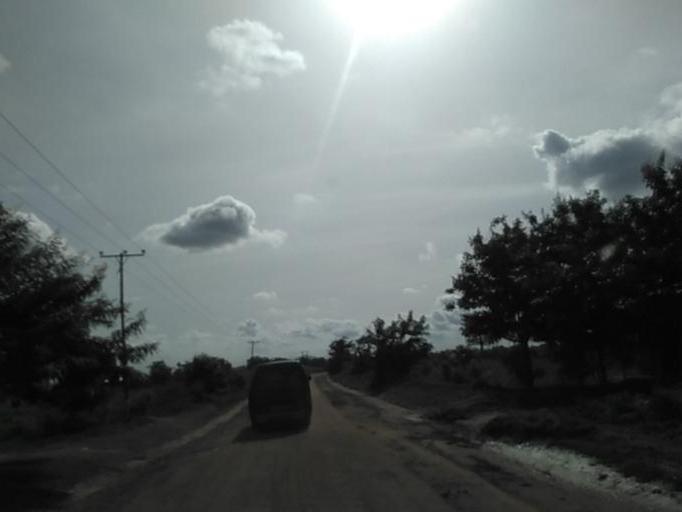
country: GH
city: Akropong
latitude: 6.0320
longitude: 0.3377
